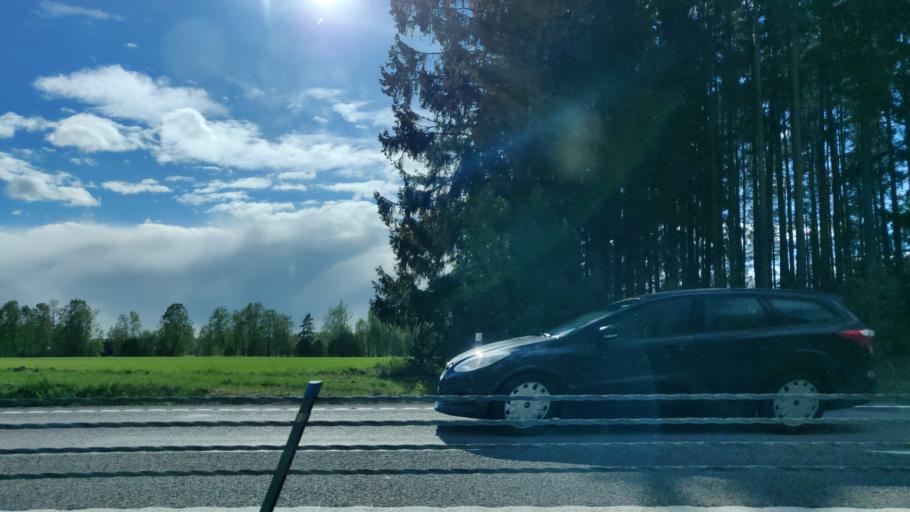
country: SE
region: Vaermland
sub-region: Forshaga Kommun
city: Forshaga
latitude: 59.4721
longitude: 13.4114
